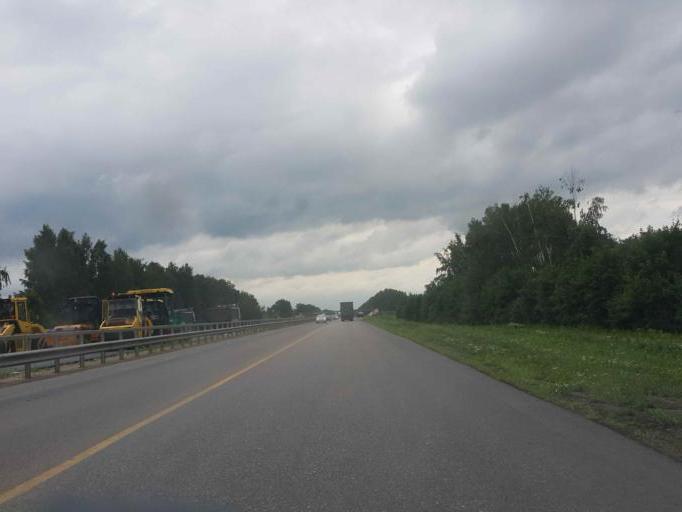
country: RU
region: Tambov
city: Selezni
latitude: 52.8055
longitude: 40.9699
